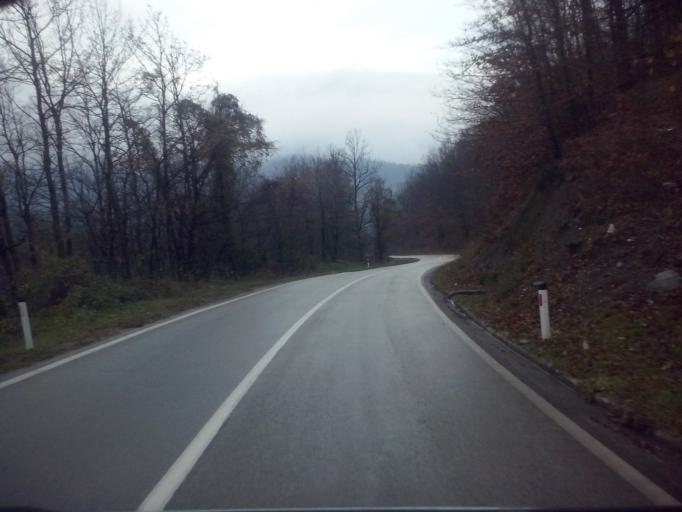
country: RS
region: Central Serbia
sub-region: Moravicki Okrug
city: Ivanjica
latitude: 43.5406
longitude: 20.2690
